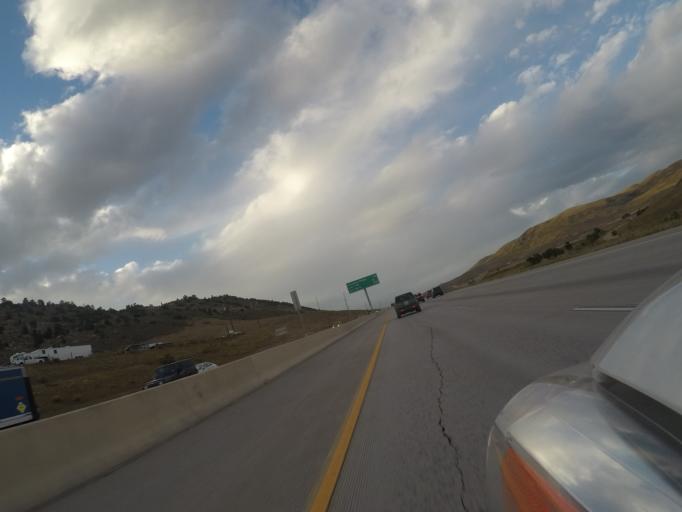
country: US
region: Colorado
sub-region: Jefferson County
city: West Pleasant View
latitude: 39.6726
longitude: -105.1881
